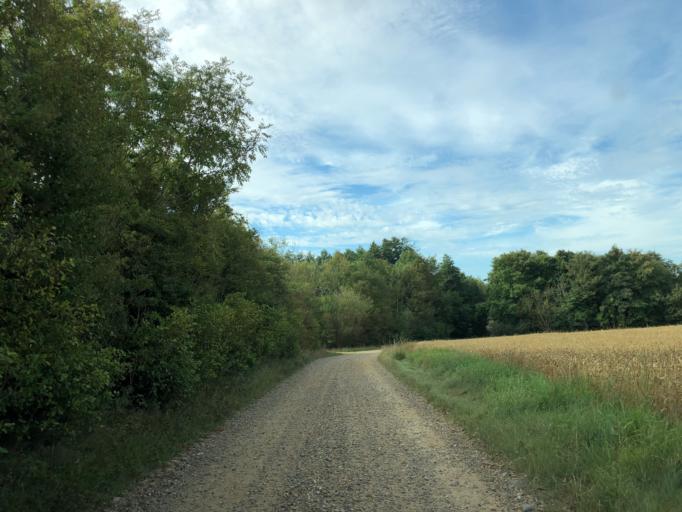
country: DK
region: Central Jutland
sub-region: Ringkobing-Skjern Kommune
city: Skjern
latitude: 56.0712
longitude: 8.4215
